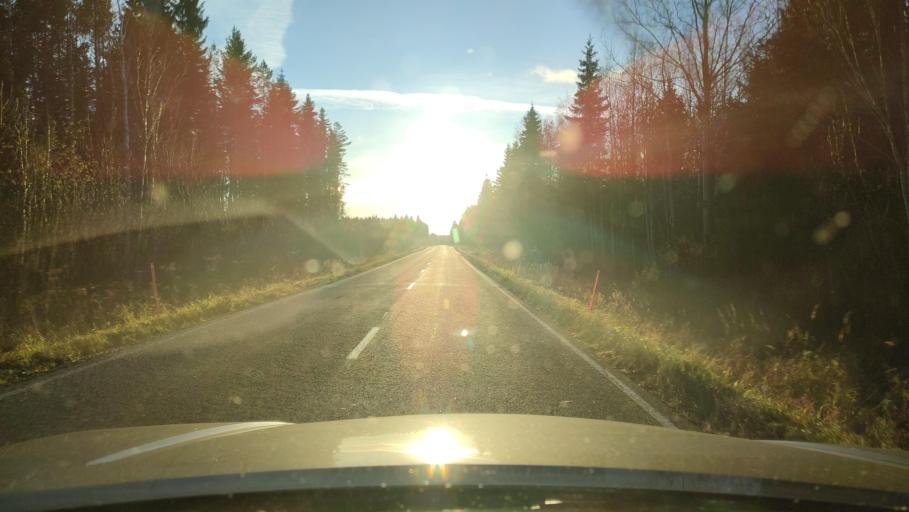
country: FI
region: Ostrobothnia
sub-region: Vaasa
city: Malax
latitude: 62.6951
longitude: 21.5668
